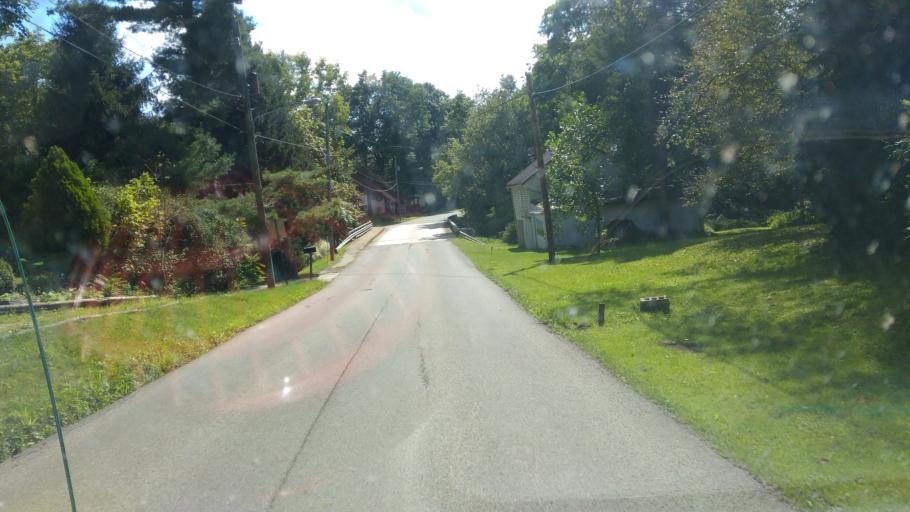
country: US
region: Ohio
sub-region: Wayne County
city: Apple Creek
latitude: 40.6726
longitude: -81.8707
